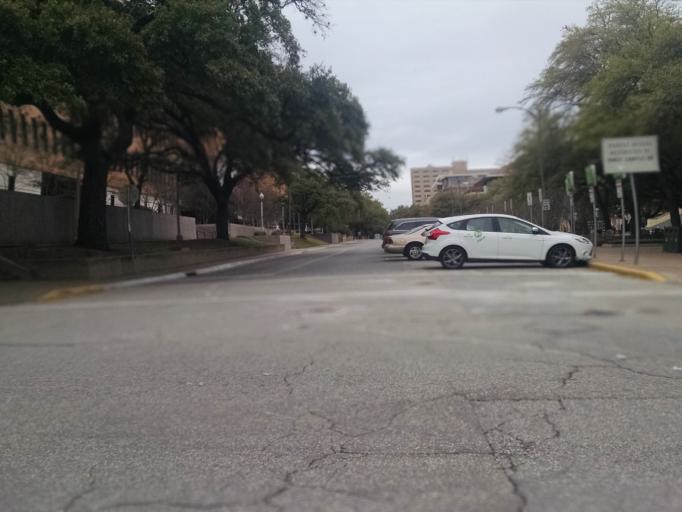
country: US
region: Texas
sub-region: Travis County
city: Austin
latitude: 30.2834
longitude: -97.7374
